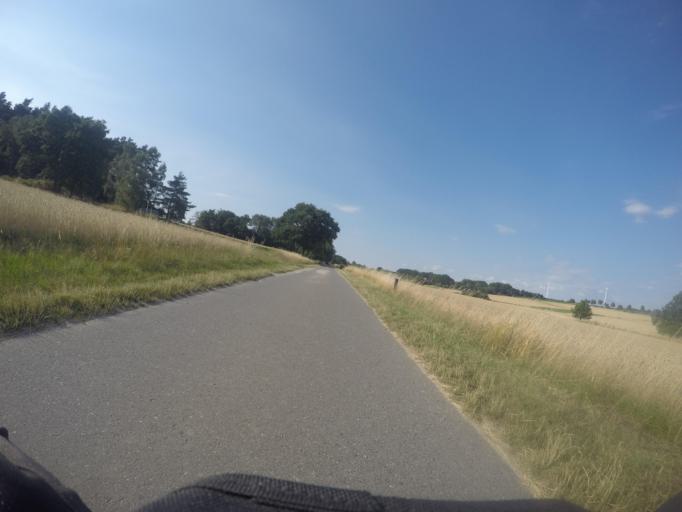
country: DE
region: Lower Saxony
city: Dahlem
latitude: 53.1977
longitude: 10.7438
